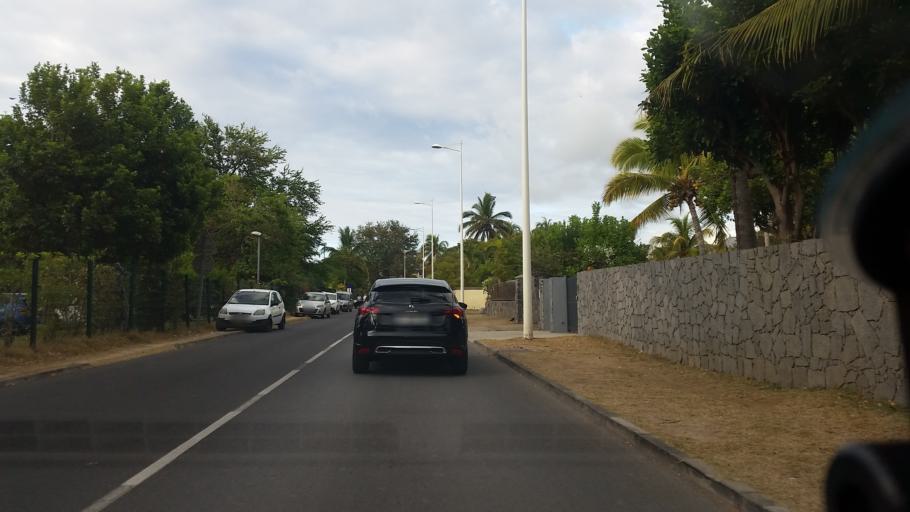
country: RE
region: Reunion
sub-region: Reunion
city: Trois-Bassins
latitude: -21.0780
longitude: 55.2229
